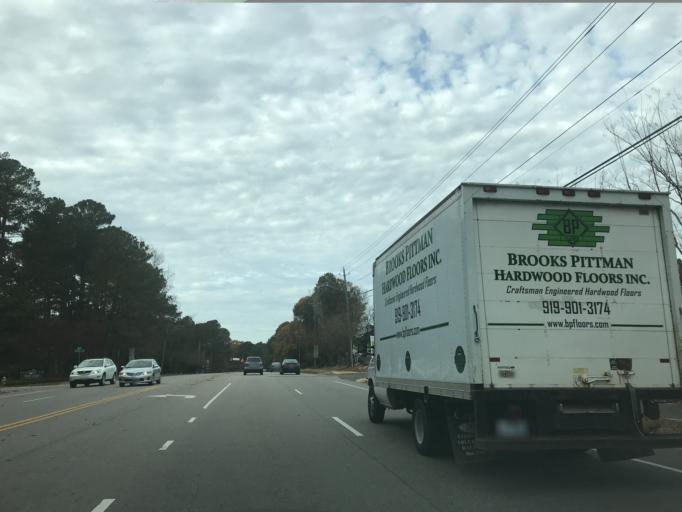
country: US
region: North Carolina
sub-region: Wake County
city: West Raleigh
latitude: 35.8671
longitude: -78.6089
